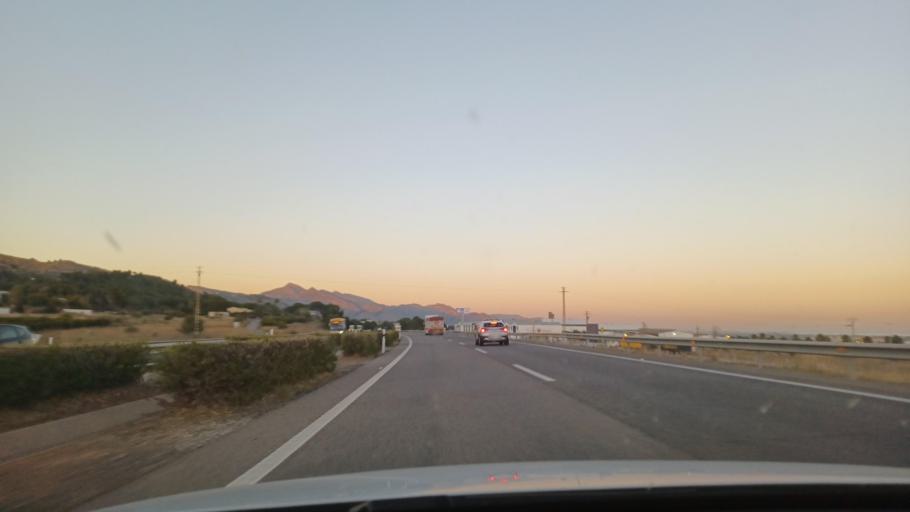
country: ES
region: Valencia
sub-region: Provincia de Castello
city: Castello de la Plana
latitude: 39.9997
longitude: -0.0699
